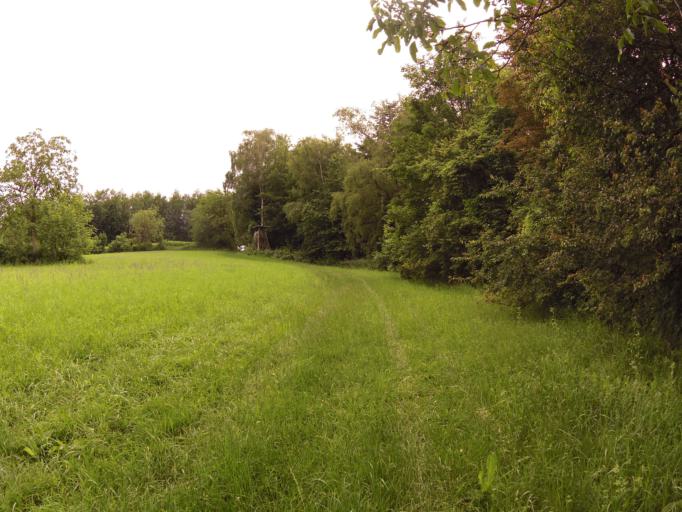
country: DE
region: Baden-Wuerttemberg
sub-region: Freiburg Region
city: Lahr
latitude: 48.3538
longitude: 7.8607
